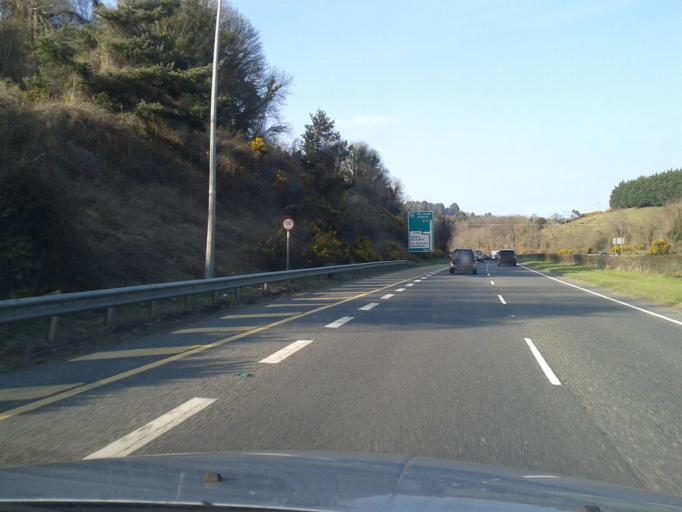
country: IE
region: Leinster
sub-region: Wicklow
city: Kilpedder
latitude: 53.1243
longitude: -6.1054
